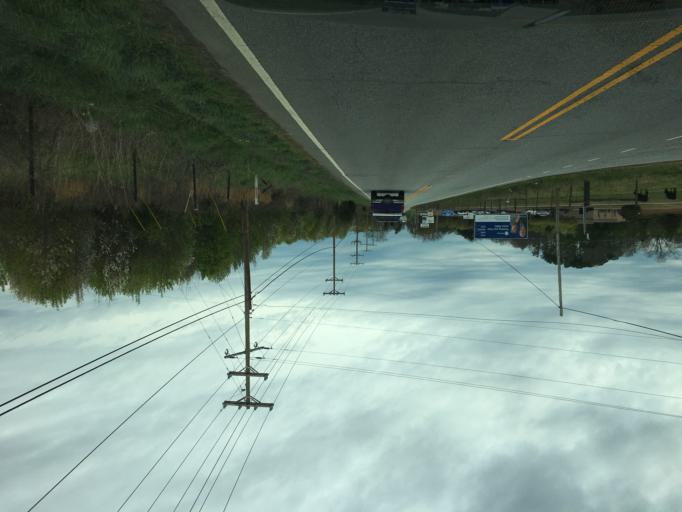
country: US
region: South Carolina
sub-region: Anderson County
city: Piedmont
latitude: 34.7040
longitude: -82.4826
